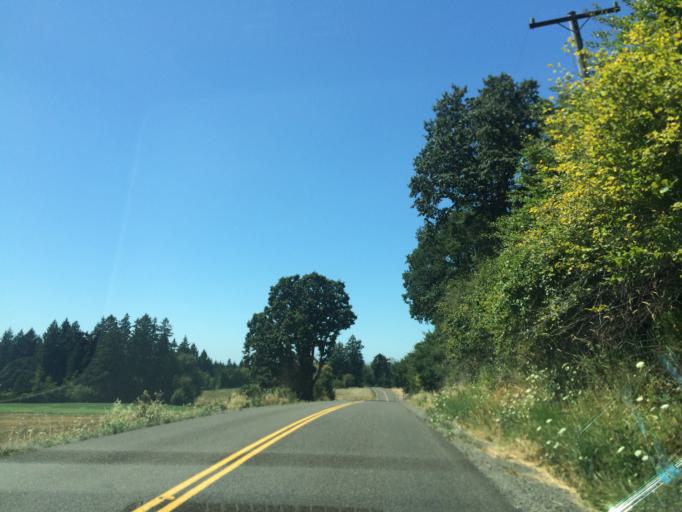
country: US
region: Oregon
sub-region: Marion County
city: Hubbard
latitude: 45.2495
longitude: -122.8549
